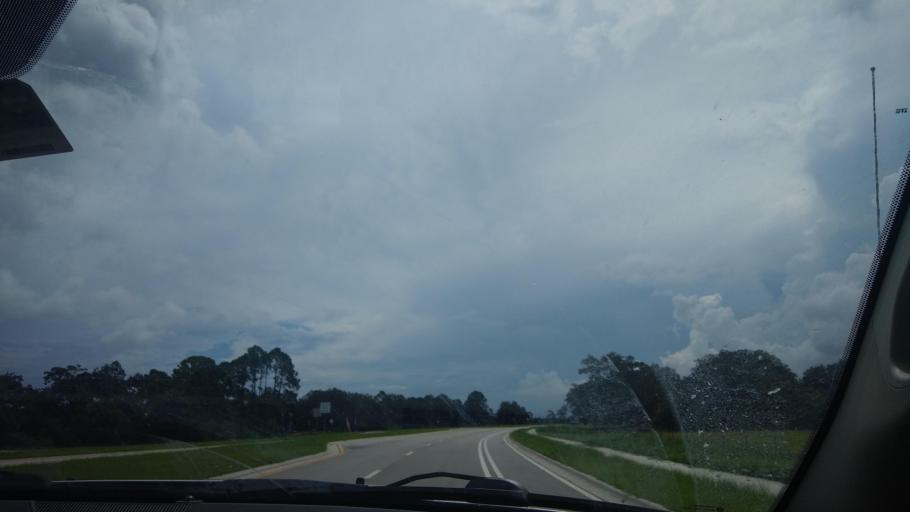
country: US
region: Florida
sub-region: Brevard County
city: Grant-Valkaria
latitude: 27.8965
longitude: -80.6159
